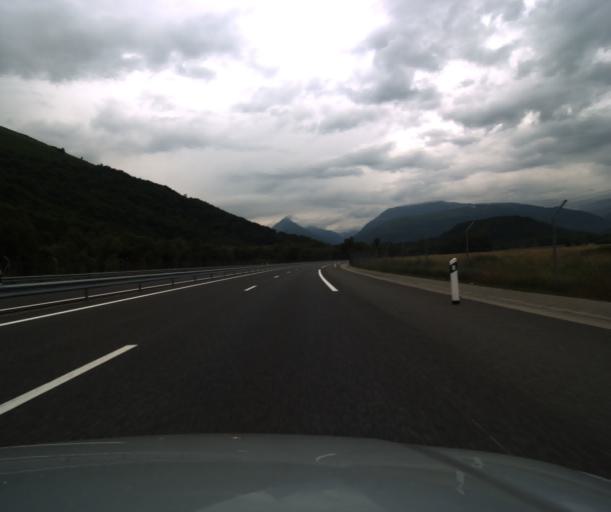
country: FR
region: Midi-Pyrenees
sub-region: Departement des Hautes-Pyrenees
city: Argeles-Gazost
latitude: 43.0344
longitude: -0.0637
